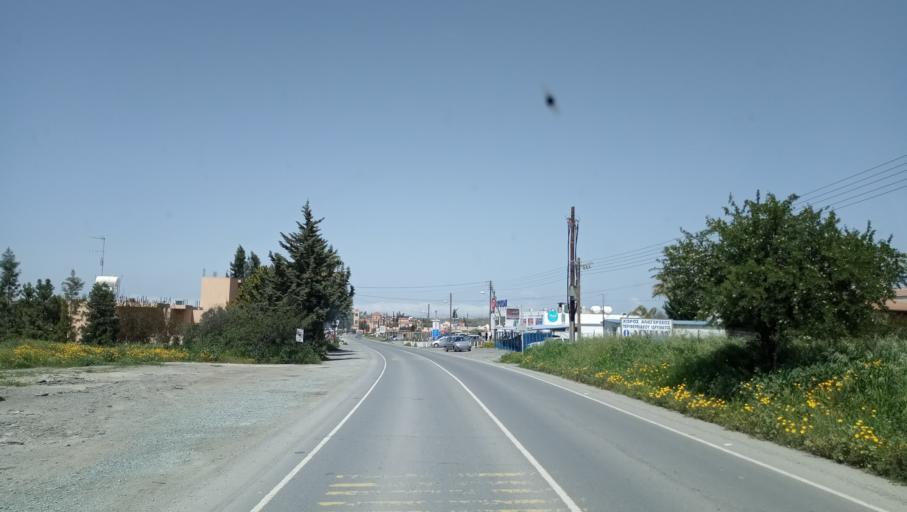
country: CY
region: Lefkosia
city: Alampra
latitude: 35.0076
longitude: 33.3940
